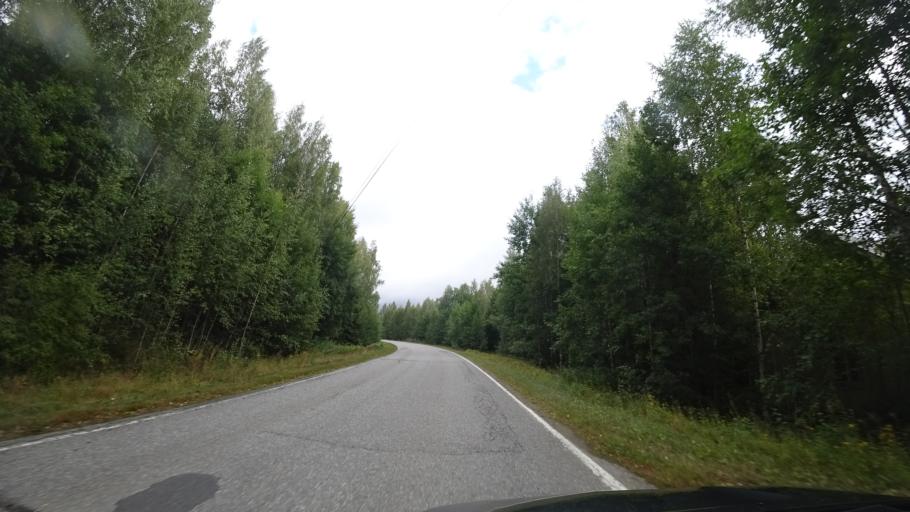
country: FI
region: Haeme
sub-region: Haemeenlinna
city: Lammi
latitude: 60.9877
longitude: 25.0218
